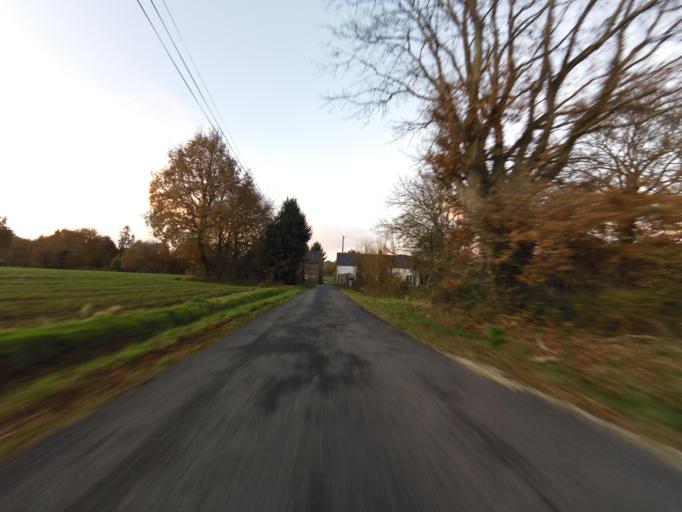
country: FR
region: Brittany
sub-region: Departement du Morbihan
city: Pluherlin
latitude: 47.7147
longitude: -2.3625
